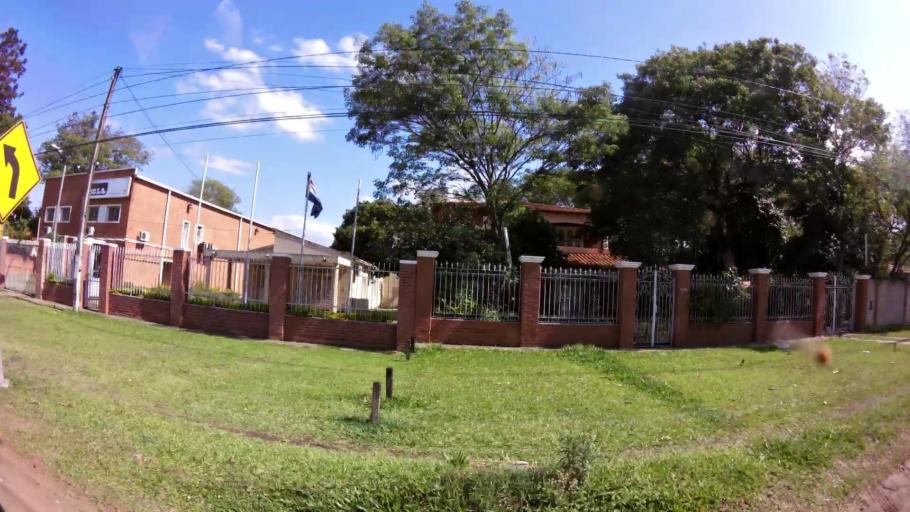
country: PY
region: Central
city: Fernando de la Mora
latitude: -25.2802
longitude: -57.5278
